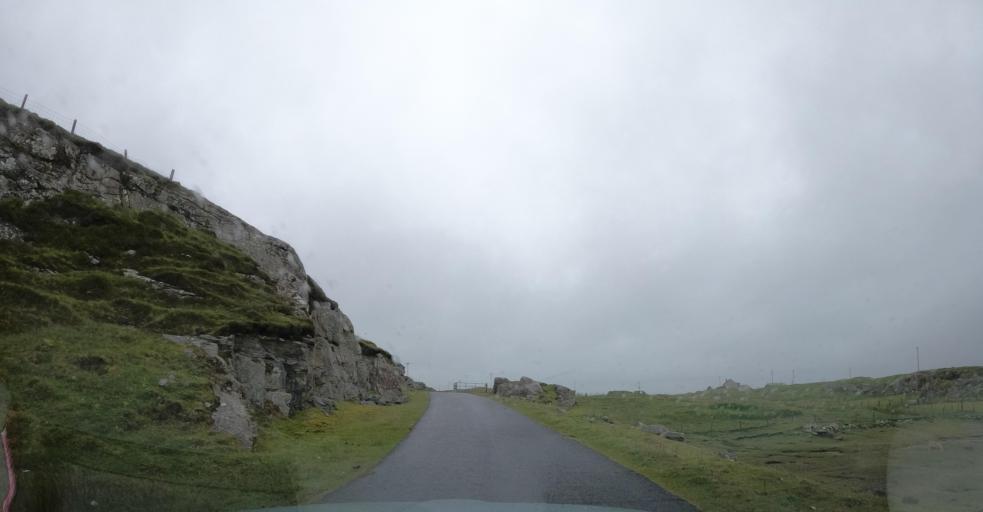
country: GB
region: Scotland
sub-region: Eilean Siar
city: Benbecula
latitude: 57.4988
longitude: -7.2456
